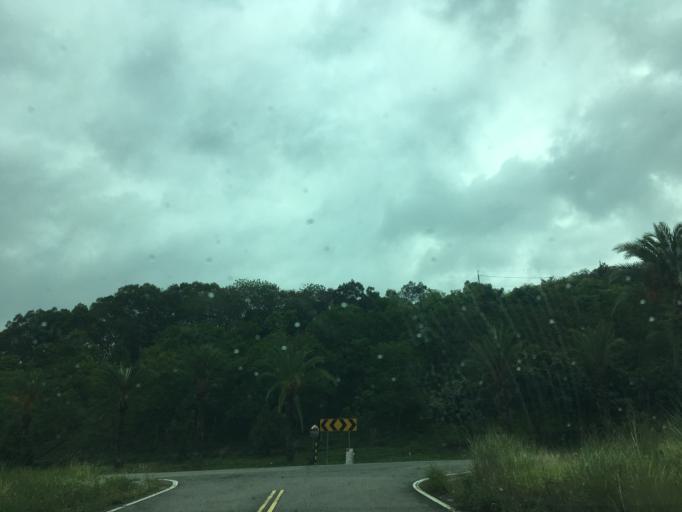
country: TW
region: Taiwan
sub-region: Taichung City
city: Taichung
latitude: 24.0570
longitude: 120.7237
